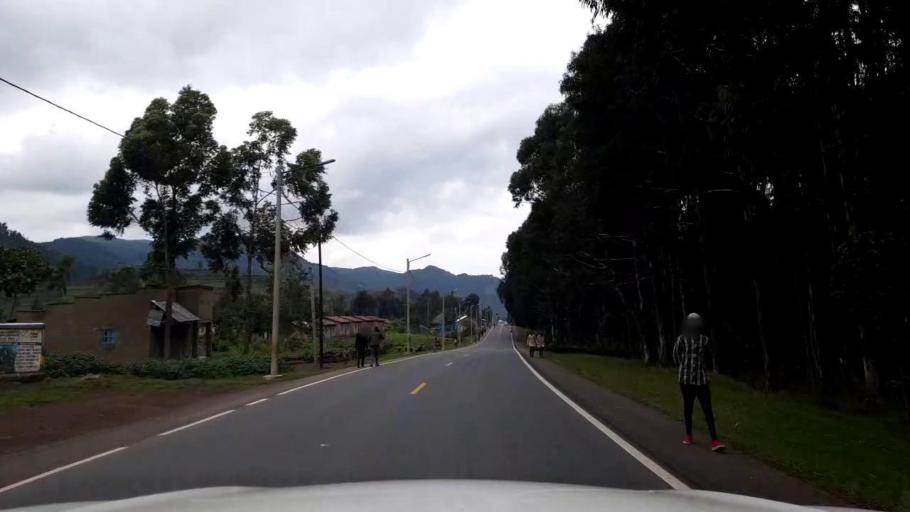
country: RW
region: Western Province
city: Gisenyi
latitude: -1.6273
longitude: 29.4218
